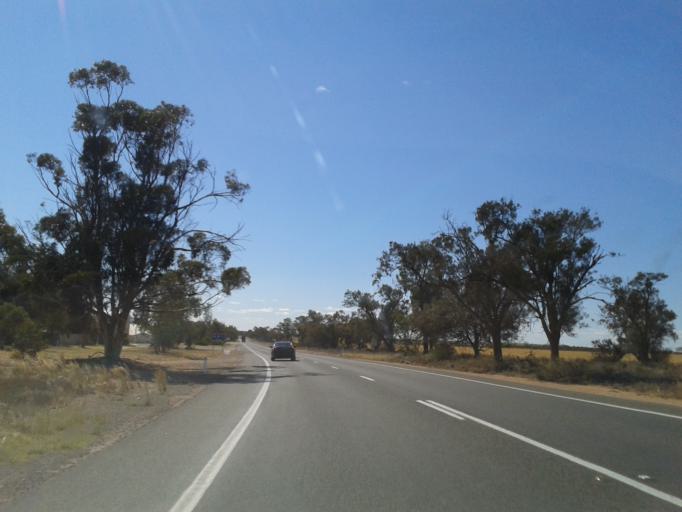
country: AU
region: New South Wales
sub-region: Wentworth
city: Dareton
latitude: -34.2782
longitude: 141.5885
